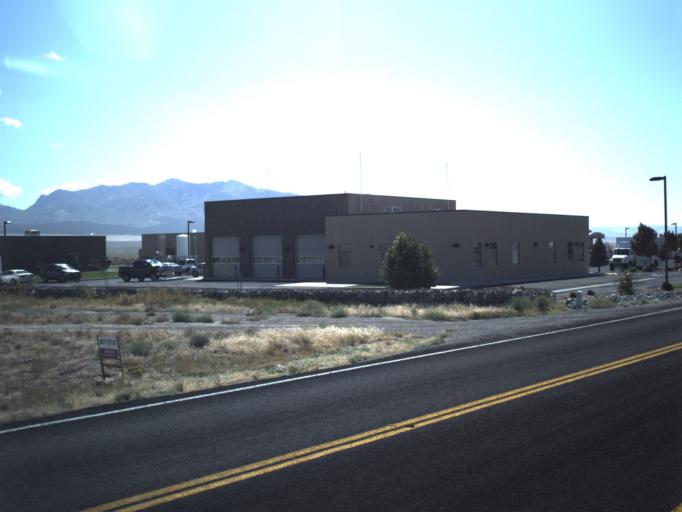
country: US
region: Utah
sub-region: Beaver County
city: Milford
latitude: 38.4084
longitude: -113.0099
